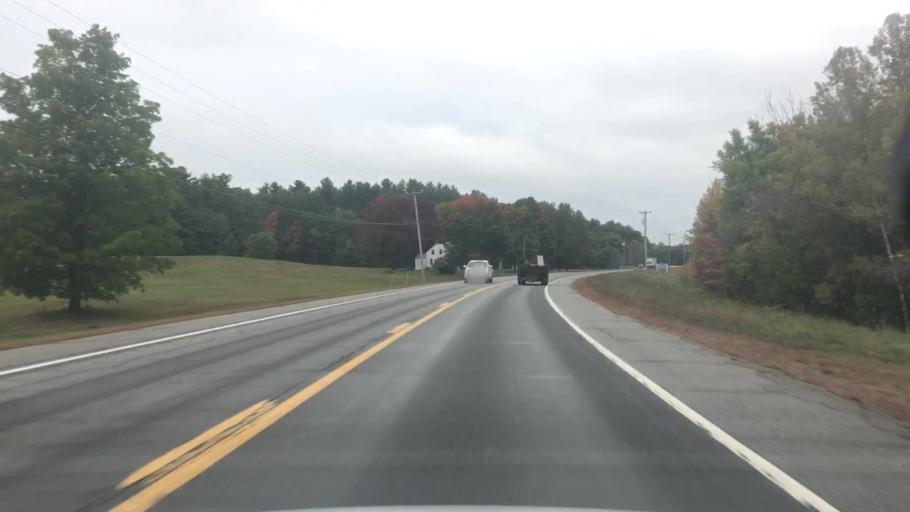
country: US
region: Maine
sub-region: Kennebec County
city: Belgrade
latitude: 44.4353
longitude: -69.8331
